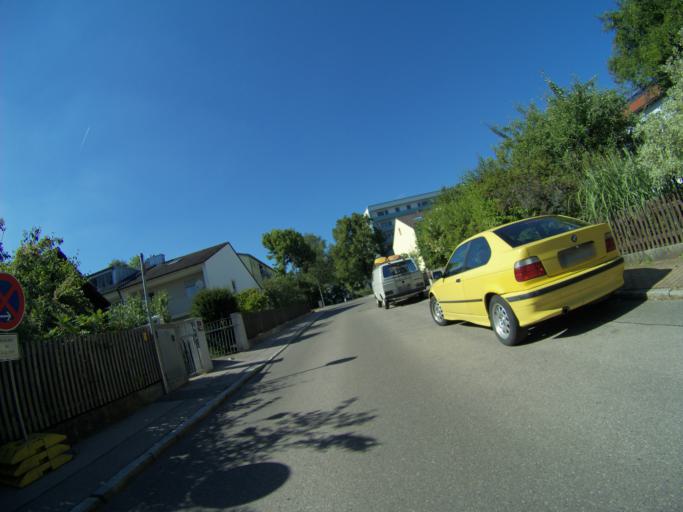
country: DE
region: Bavaria
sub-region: Upper Bavaria
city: Freising
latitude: 48.3965
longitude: 11.7104
